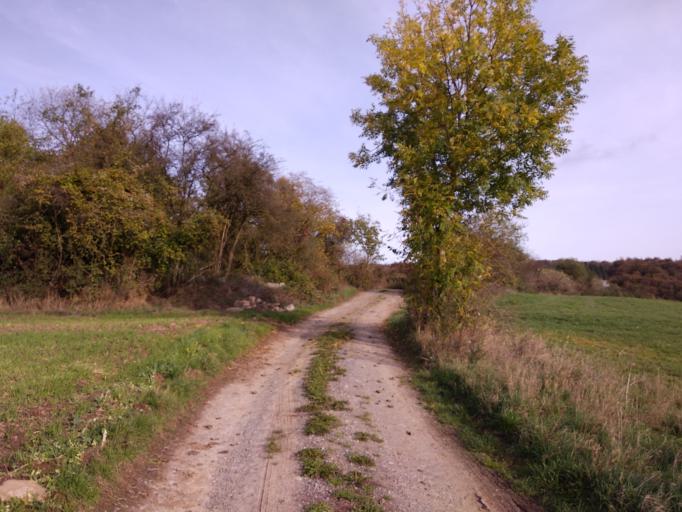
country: DE
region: North Rhine-Westphalia
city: Beverungen
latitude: 51.6832
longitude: 9.3530
